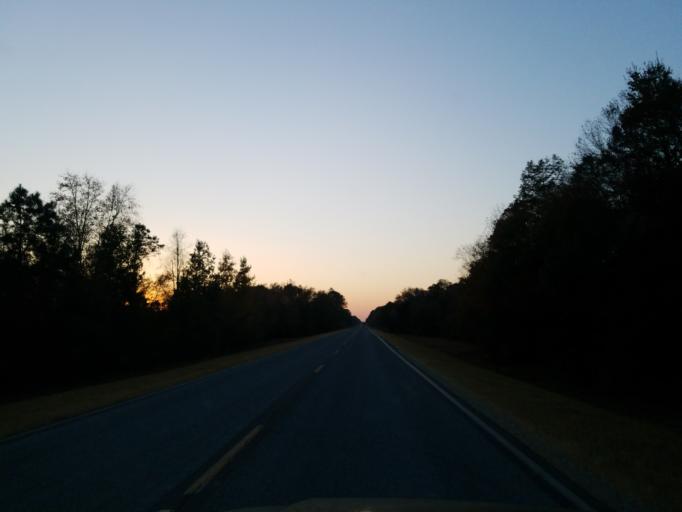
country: US
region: Georgia
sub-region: Ben Hill County
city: Fitzgerald
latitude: 31.7210
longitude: -83.4470
